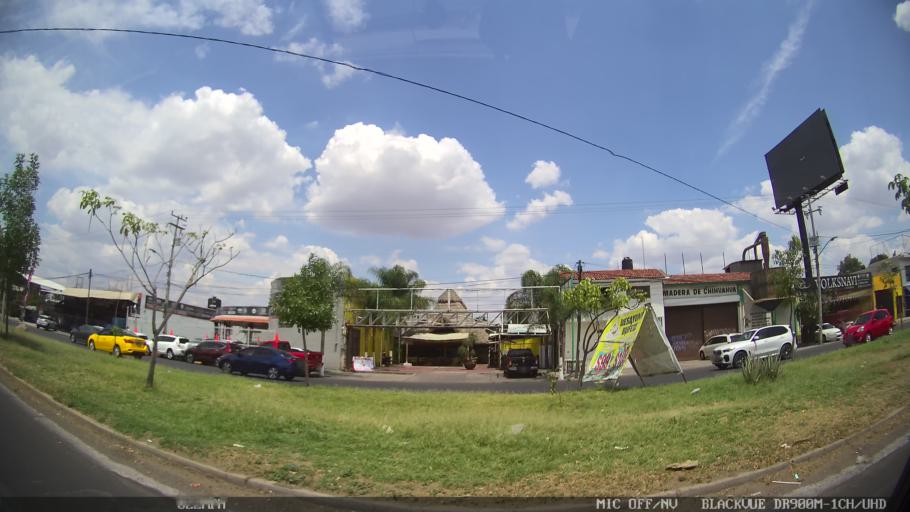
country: MX
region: Jalisco
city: Tlaquepaque
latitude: 20.6429
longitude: -103.2813
